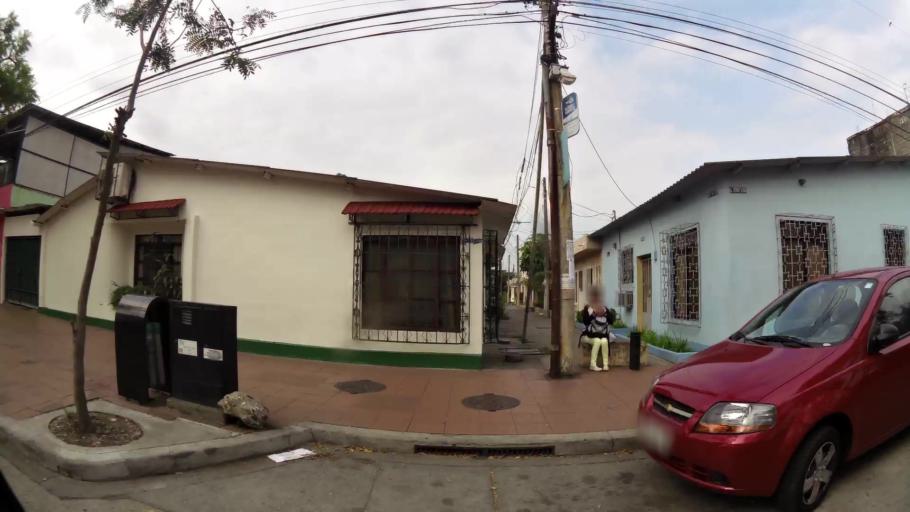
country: EC
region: Guayas
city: Eloy Alfaro
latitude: -2.1392
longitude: -79.8907
